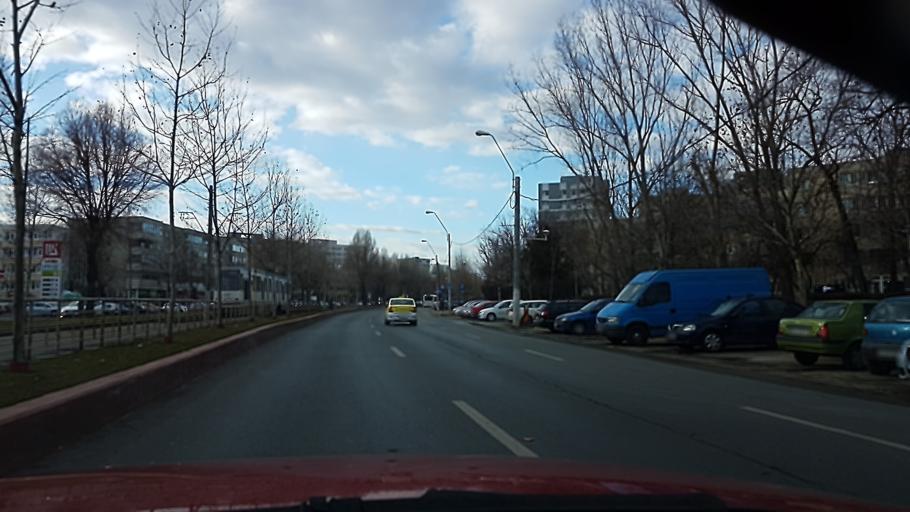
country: RO
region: Ilfov
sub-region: Comuna Popesti-Leordeni
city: Popesti-Leordeni
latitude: 44.4136
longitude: 26.1576
